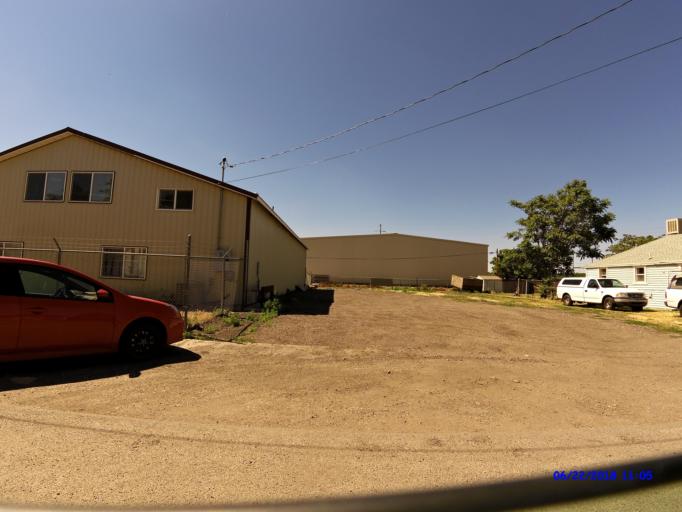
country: US
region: Utah
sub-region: Weber County
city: Ogden
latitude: 41.2282
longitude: -111.9818
